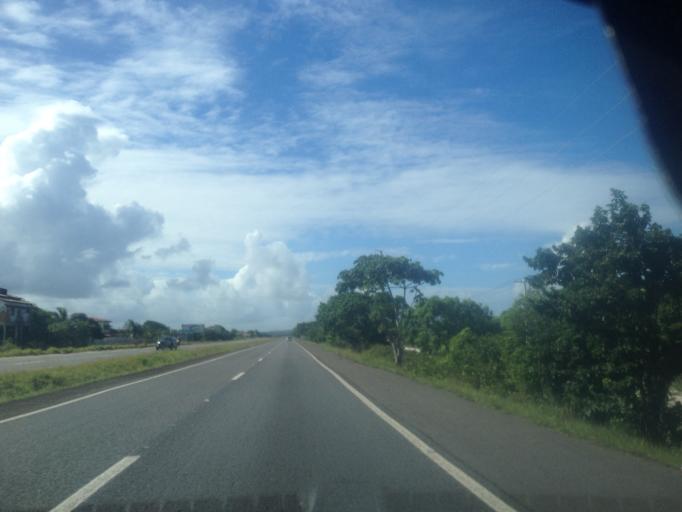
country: BR
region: Bahia
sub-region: Mata De Sao Joao
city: Mata de Sao Joao
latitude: -12.6322
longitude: -38.0661
